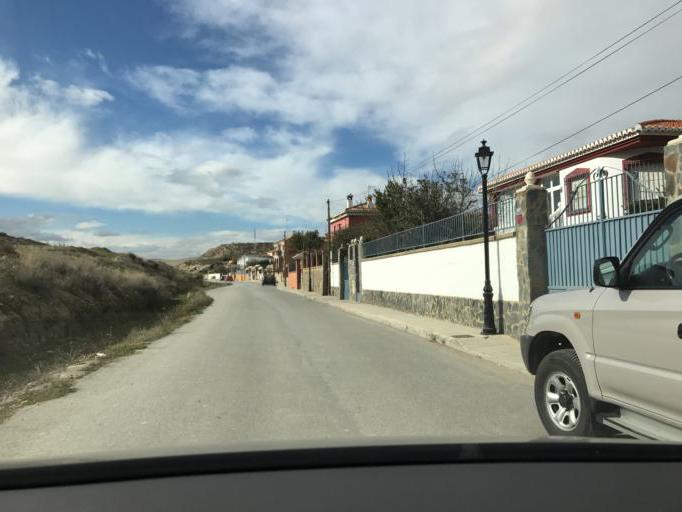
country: ES
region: Andalusia
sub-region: Provincia de Granada
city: Alhendin
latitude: 37.1053
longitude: -3.6640
